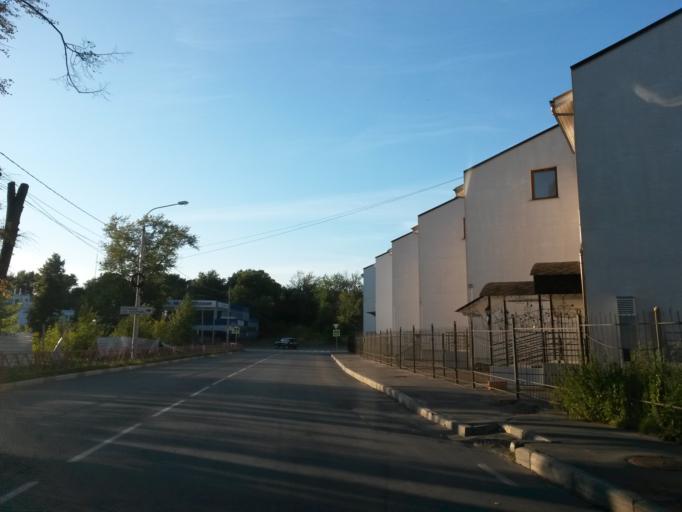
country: RU
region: Jaroslavl
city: Yaroslavl
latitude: 57.6115
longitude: 39.8805
